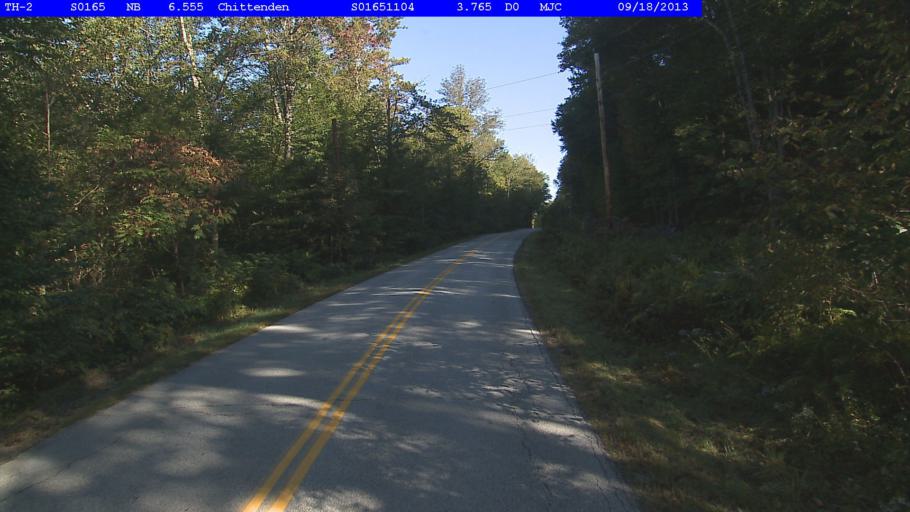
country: US
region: Vermont
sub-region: Rutland County
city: Rutland
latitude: 43.7282
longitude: -72.9708
